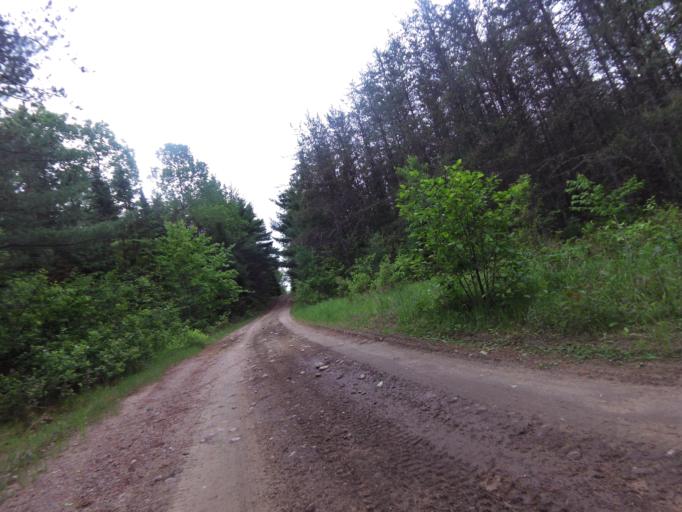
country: CA
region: Quebec
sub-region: Outaouais
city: Shawville
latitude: 45.9085
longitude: -76.2979
